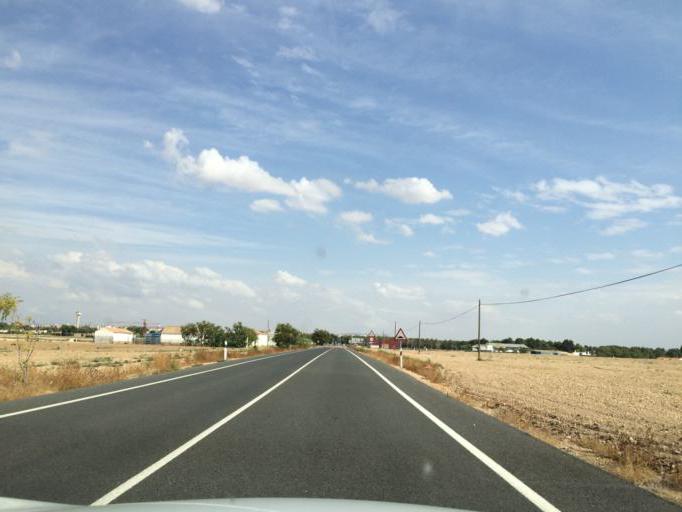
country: ES
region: Castille-La Mancha
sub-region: Provincia de Albacete
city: Albacete
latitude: 38.9997
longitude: -1.8987
